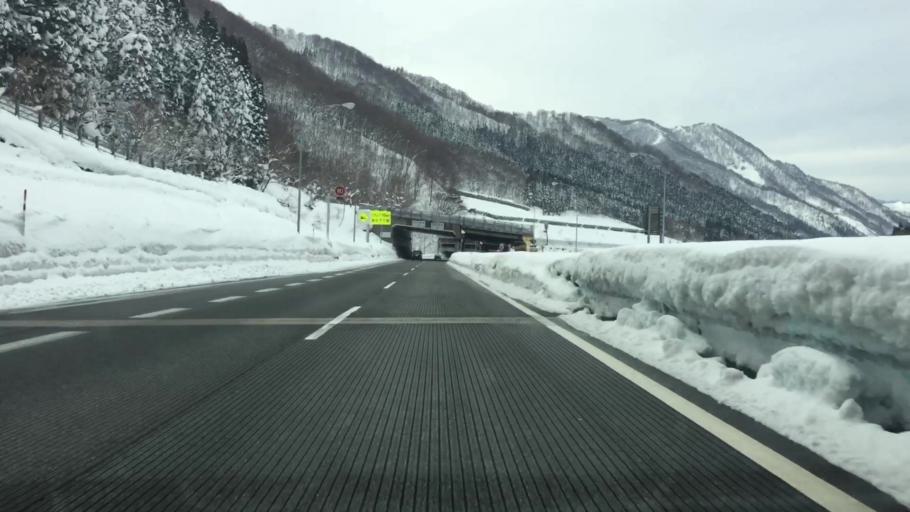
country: JP
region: Niigata
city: Shiozawa
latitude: 36.8665
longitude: 138.8718
